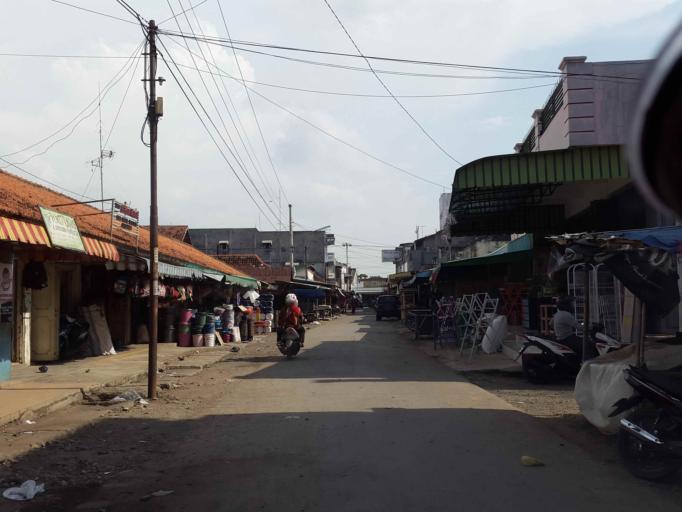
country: ID
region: Central Java
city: Dukuhturi
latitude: -6.9650
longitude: 109.0562
